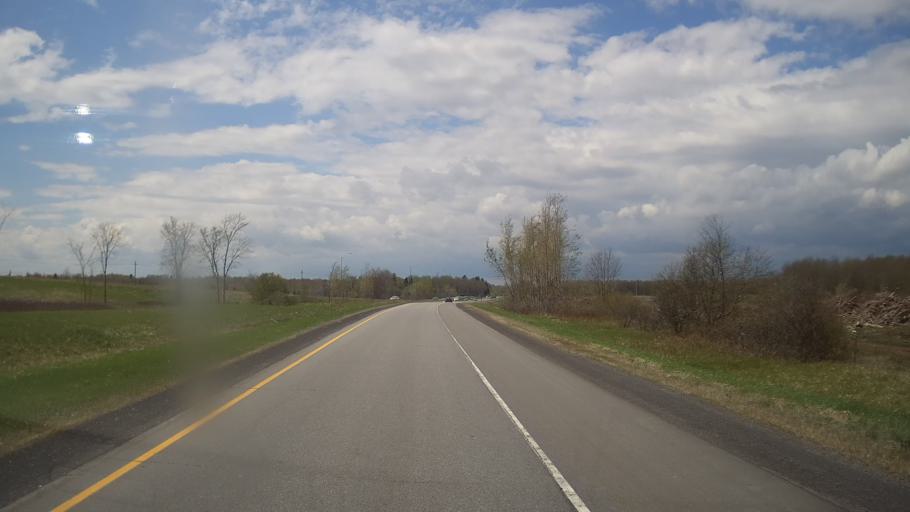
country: CA
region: Ontario
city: Hawkesbury
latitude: 45.5668
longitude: -74.5041
